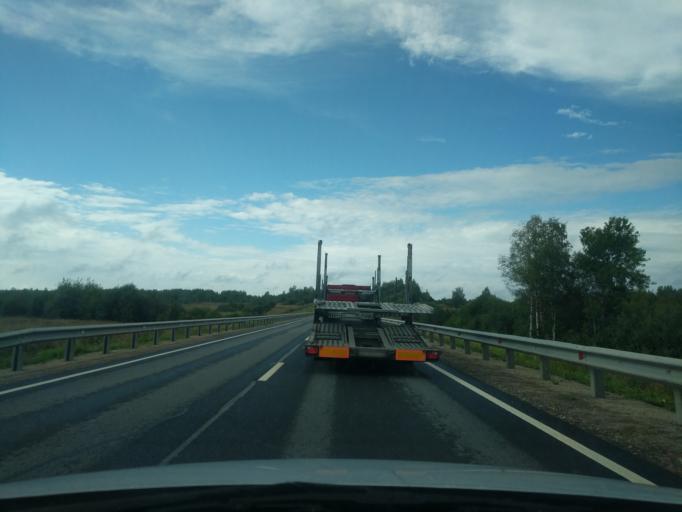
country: RU
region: Kostroma
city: Sudislavl'
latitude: 57.8171
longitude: 41.9509
